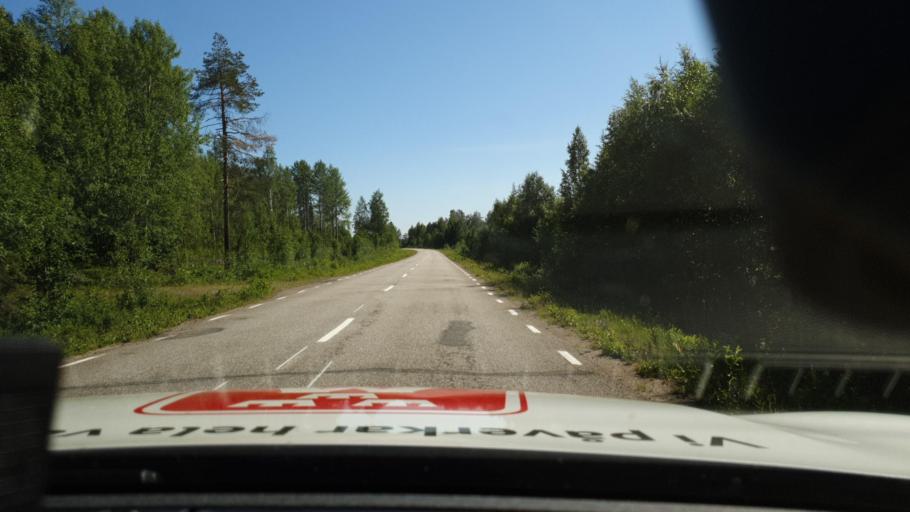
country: SE
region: Norrbotten
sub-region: Lulea Kommun
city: Ranea
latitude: 66.0253
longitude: 22.2979
